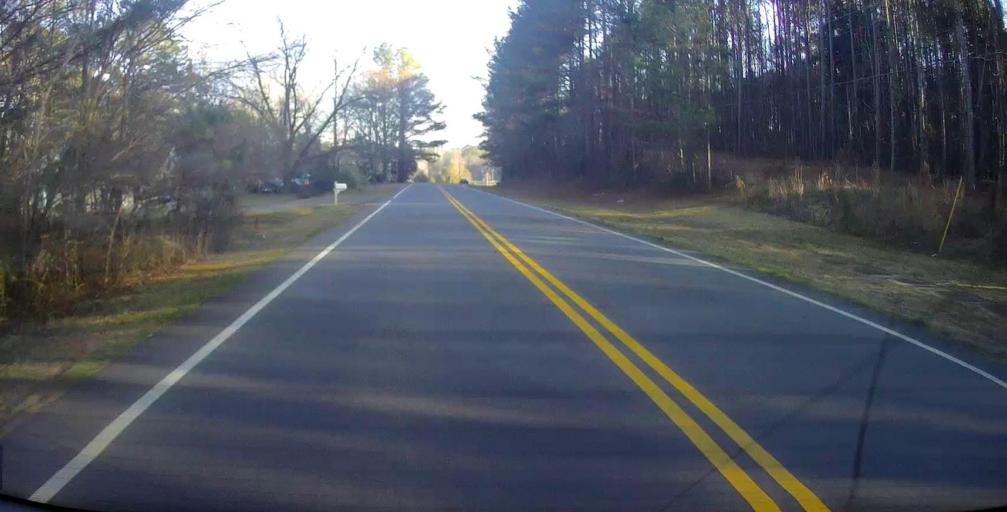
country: US
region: Georgia
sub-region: Meriwether County
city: Manchester
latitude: 32.8870
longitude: -84.6763
